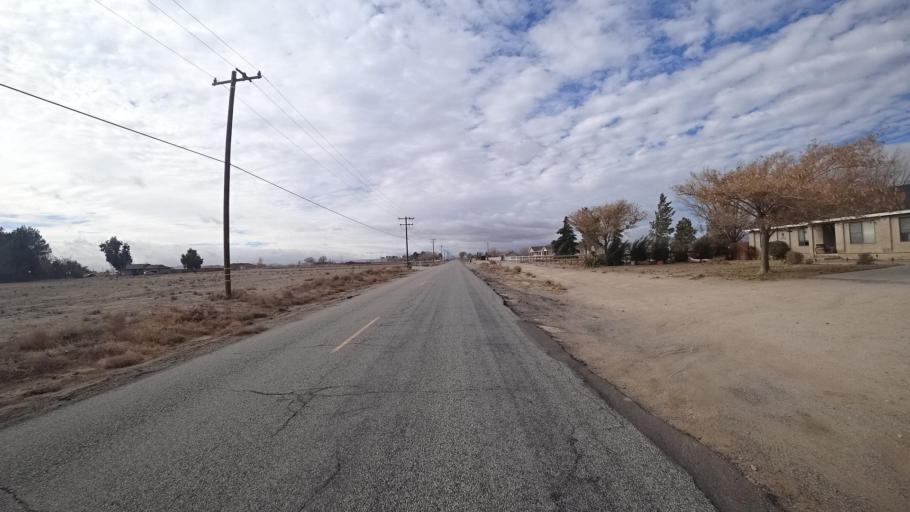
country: US
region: California
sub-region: Kern County
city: Rosamond
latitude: 34.8201
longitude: -118.2674
